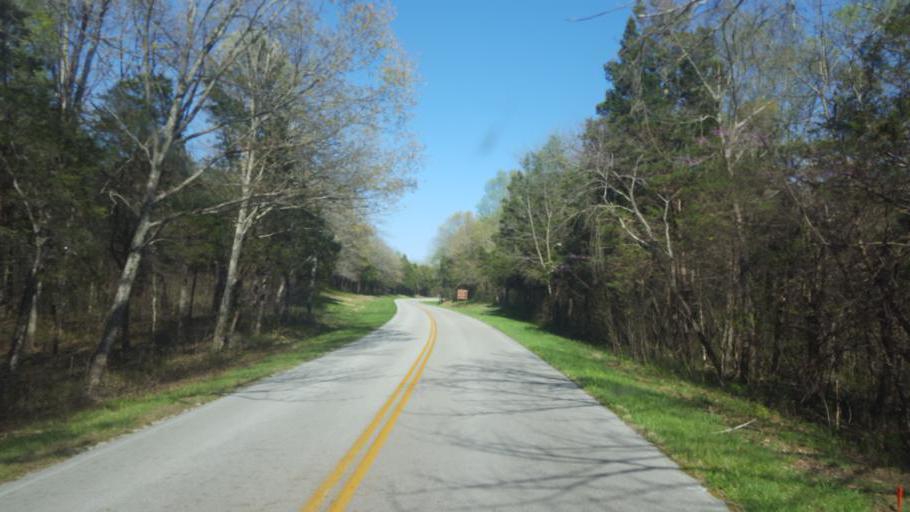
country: US
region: Kentucky
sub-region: Barren County
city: Cave City
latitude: 37.1525
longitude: -86.1064
